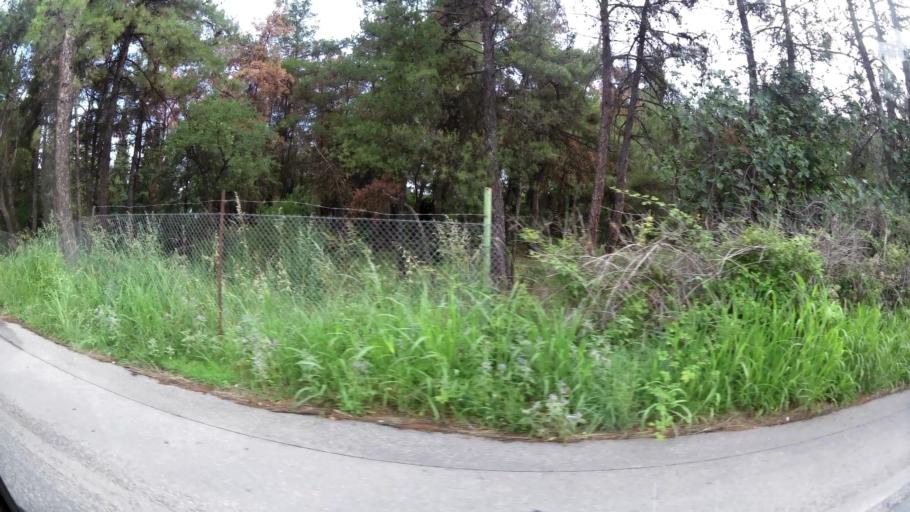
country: GR
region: Central Macedonia
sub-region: Nomos Thessalonikis
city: Panorama
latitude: 40.5916
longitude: 23.0182
